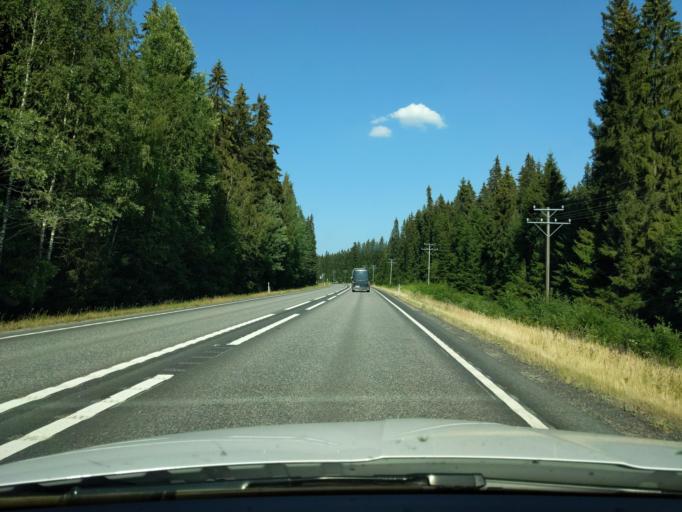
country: FI
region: Paijanne Tavastia
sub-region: Lahti
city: Hollola
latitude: 60.9396
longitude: 25.4000
